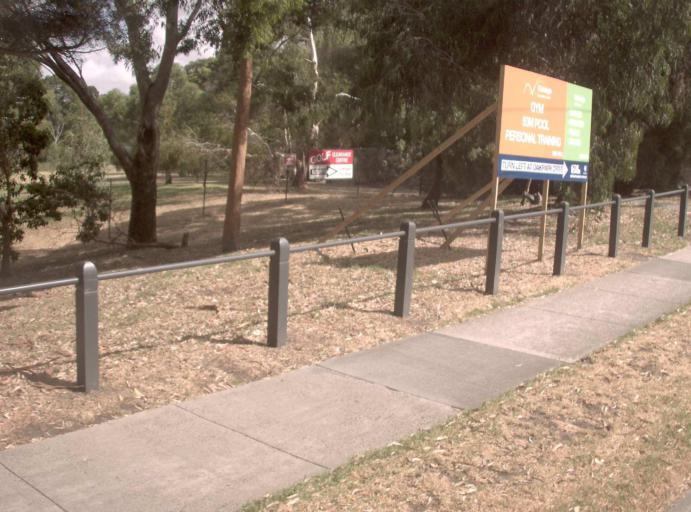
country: AU
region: Victoria
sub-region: Monash
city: Chadstone
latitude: -37.8923
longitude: 145.1071
